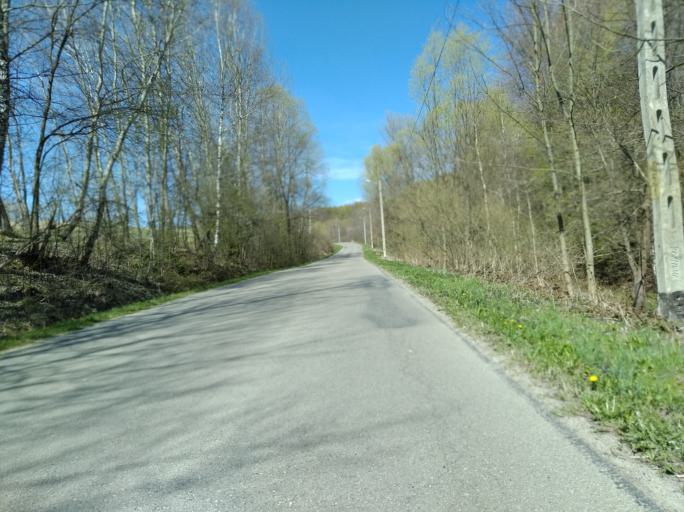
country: PL
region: Subcarpathian Voivodeship
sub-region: Powiat brzozowski
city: Golcowa
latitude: 49.7546
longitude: 22.0673
